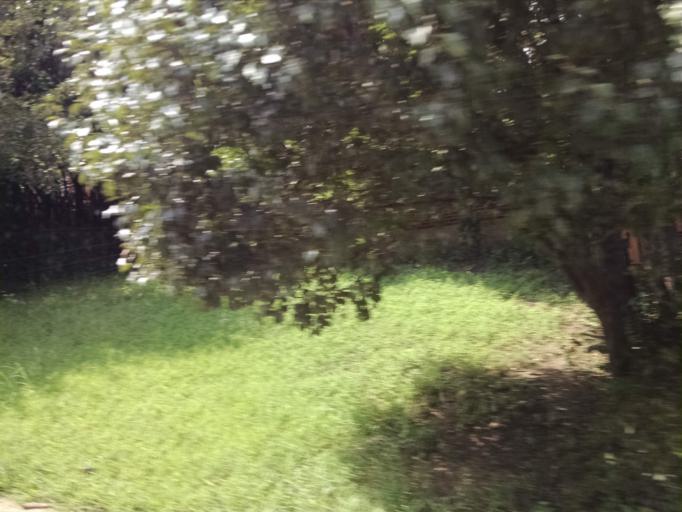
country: US
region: Illinois
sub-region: Madison County
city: Venice
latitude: 38.6723
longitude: -90.2055
